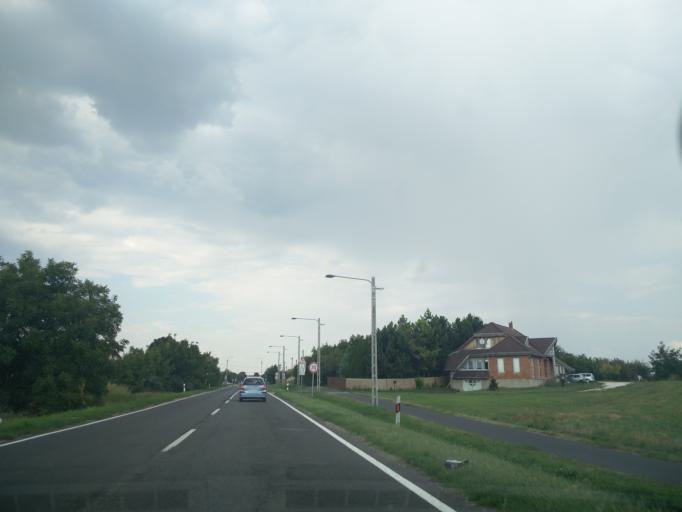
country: HU
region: Fejer
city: Polgardi
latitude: 47.0565
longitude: 18.3063
